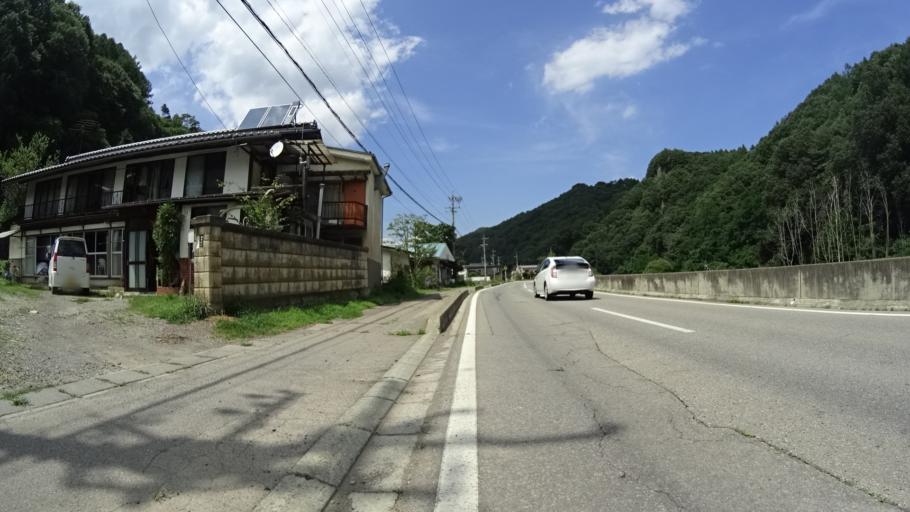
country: JP
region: Nagano
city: Saku
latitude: 36.0694
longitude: 138.4974
